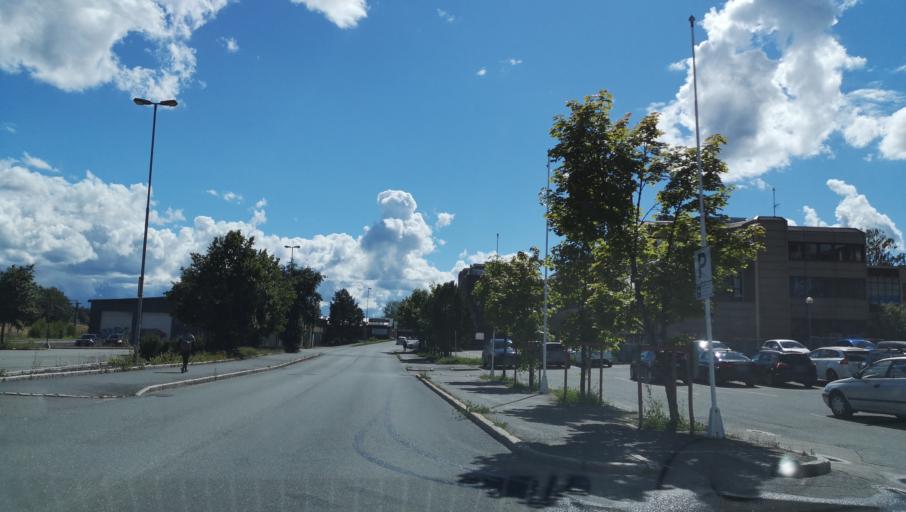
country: NO
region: Akershus
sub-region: As
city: As
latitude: 59.6625
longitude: 10.7940
